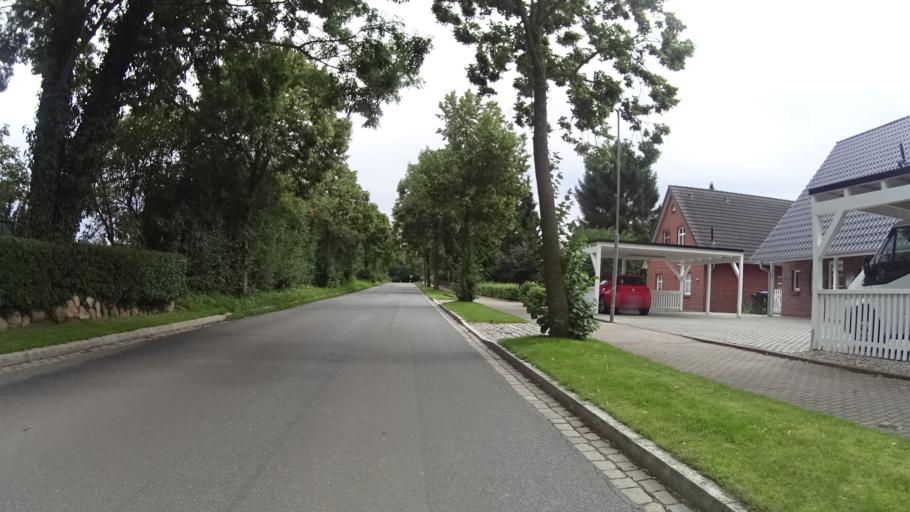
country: DE
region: Schleswig-Holstein
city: Duvensee
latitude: 53.6918
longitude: 10.5689
